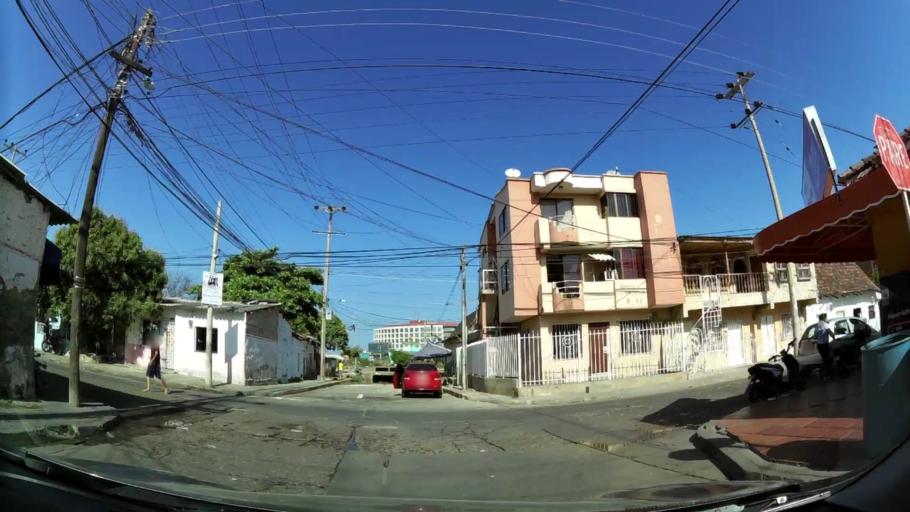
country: CO
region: Bolivar
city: Cartagena
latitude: 10.4274
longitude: -75.5378
